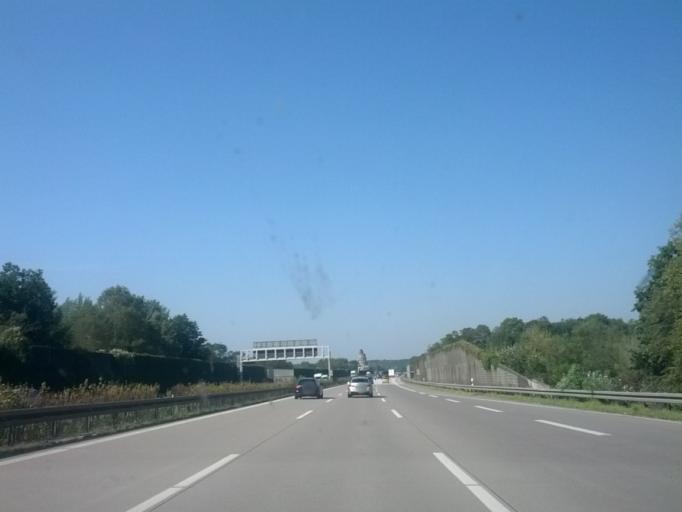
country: DE
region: Brandenburg
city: Wildau
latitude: 52.3120
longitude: 13.6575
